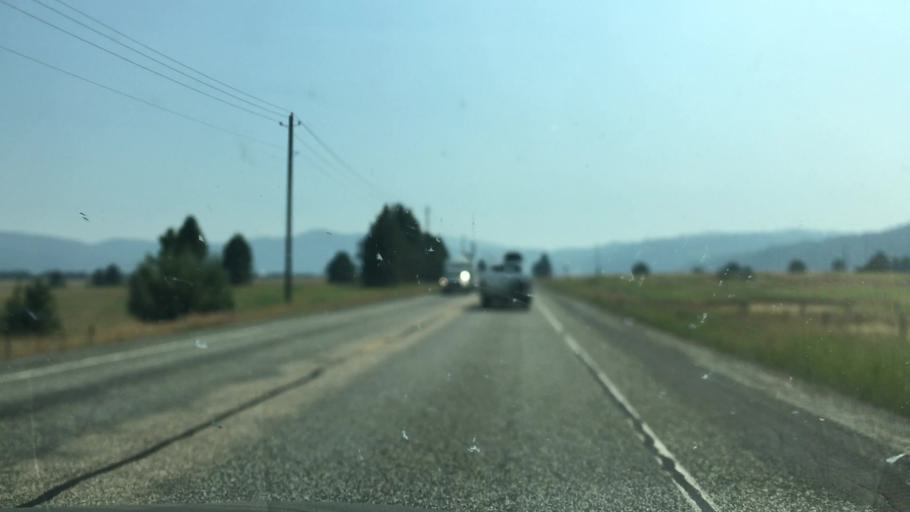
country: US
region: Idaho
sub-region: Valley County
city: Cascade
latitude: 44.3559
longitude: -116.0229
